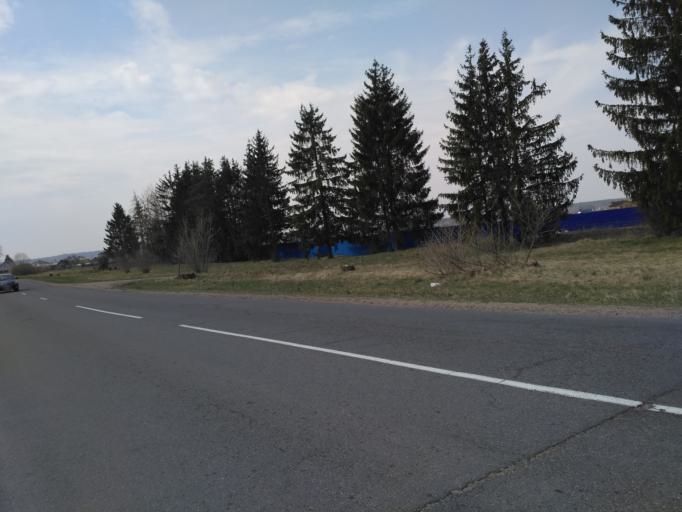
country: BY
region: Minsk
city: Zamostochcha
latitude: 53.8929
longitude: 27.9257
